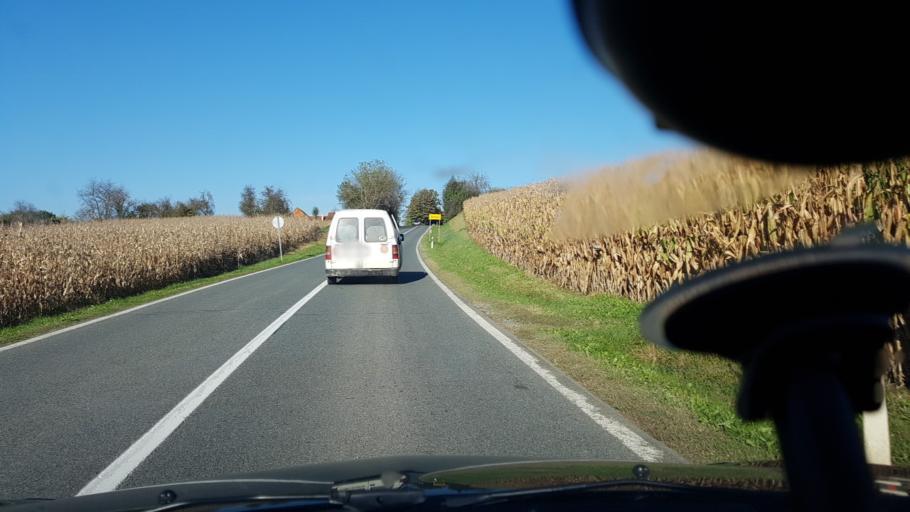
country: HR
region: Bjelovarsko-Bilogorska
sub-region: Grad Cazma
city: Cazma
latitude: 45.7943
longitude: 16.6958
